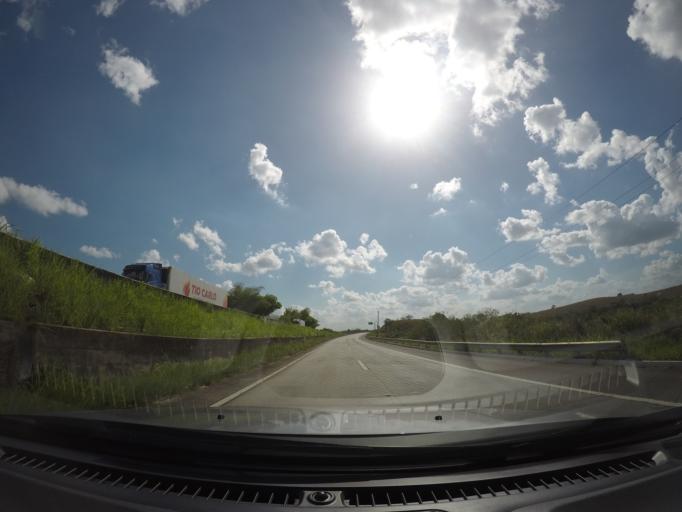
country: BR
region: Pernambuco
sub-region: Ribeirao
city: Ribeirao
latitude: -8.4511
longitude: -35.3545
